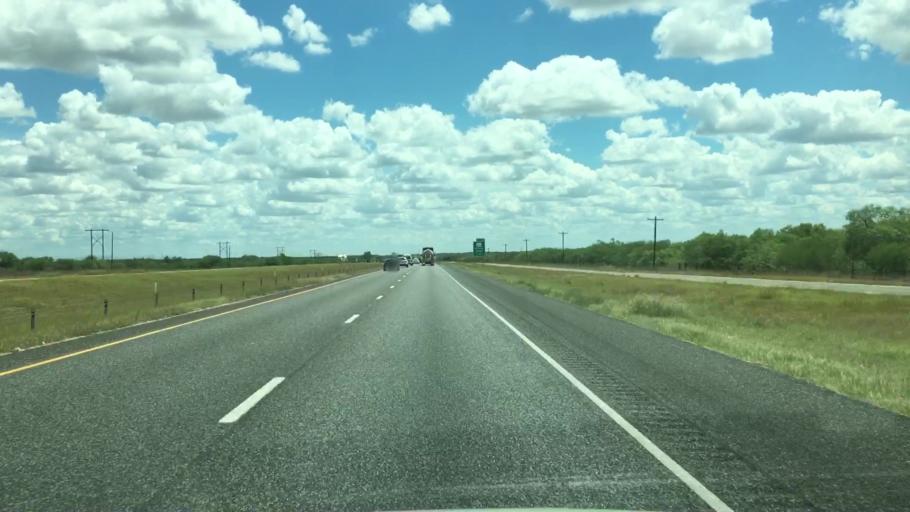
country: US
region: Texas
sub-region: Atascosa County
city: Pleasanton
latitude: 28.8611
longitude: -98.3879
